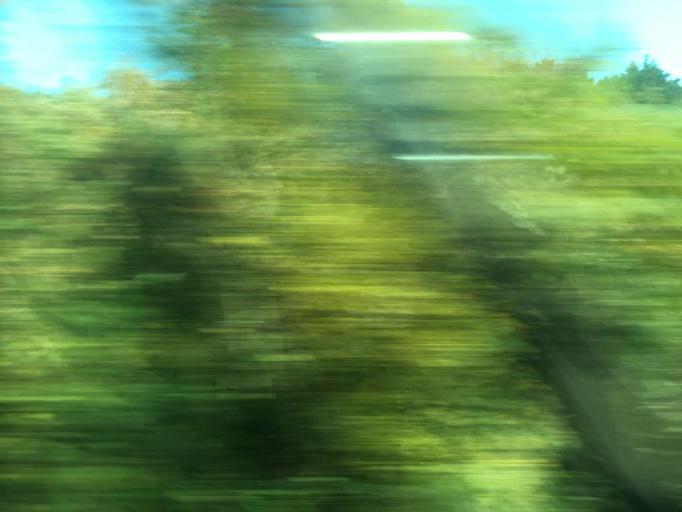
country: JP
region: Ibaraki
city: Ishioka
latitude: 36.2161
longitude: 140.2835
